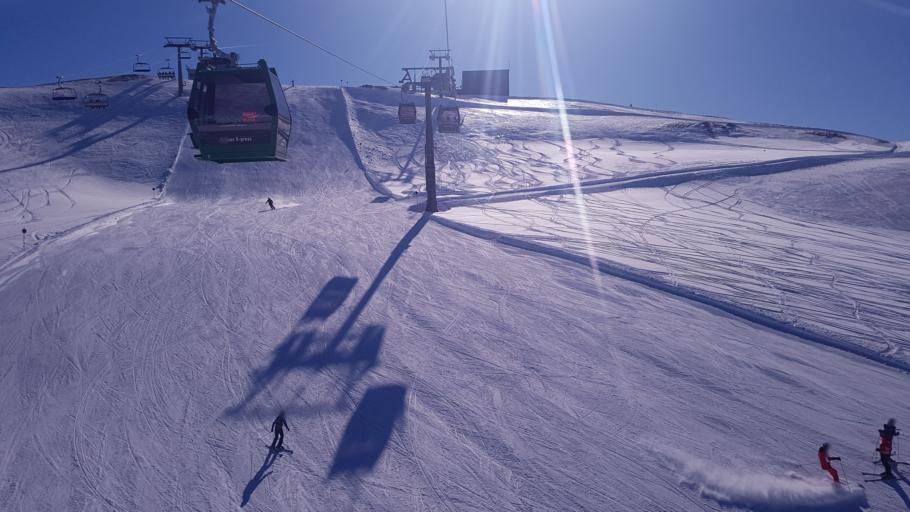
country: AT
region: Salzburg
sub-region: Politischer Bezirk Zell am See
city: Neukirchen am Grossvenediger
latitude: 47.2841
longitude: 12.2867
